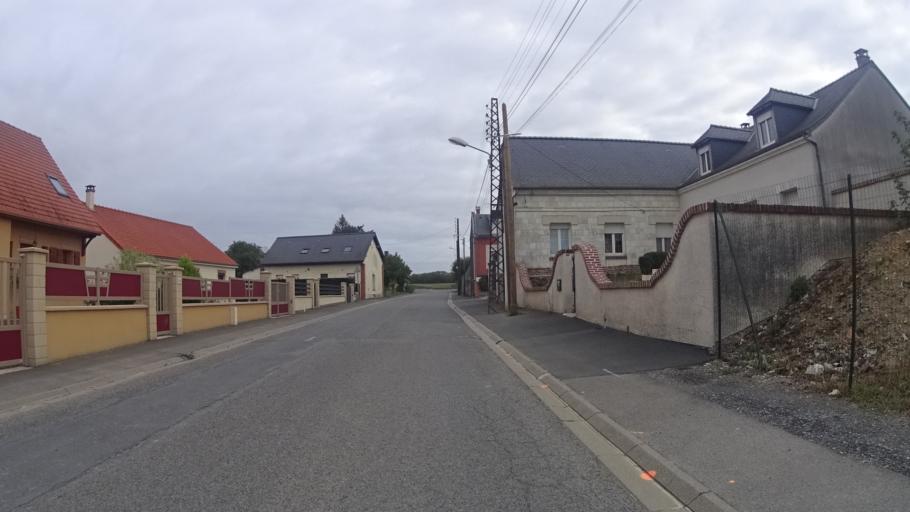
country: FR
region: Picardie
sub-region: Departement de l'Aisne
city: Guise
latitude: 49.8872
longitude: 3.5539
